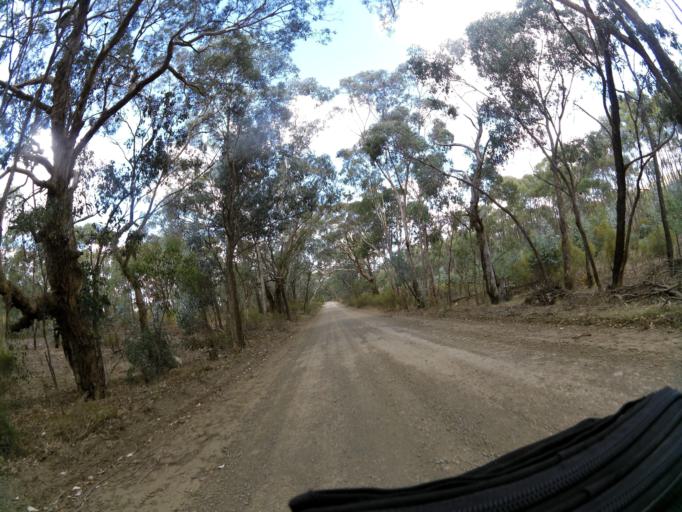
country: AU
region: Victoria
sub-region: Greater Bendigo
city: Kennington
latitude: -36.9624
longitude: 144.7799
